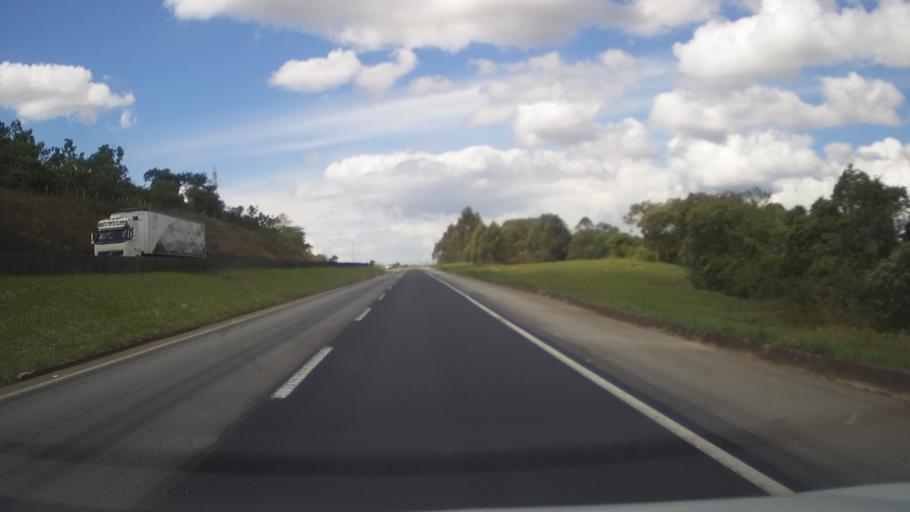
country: BR
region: Minas Gerais
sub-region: Santo Antonio Do Amparo
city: Santo Antonio do Amparo
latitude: -20.8413
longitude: -44.8261
